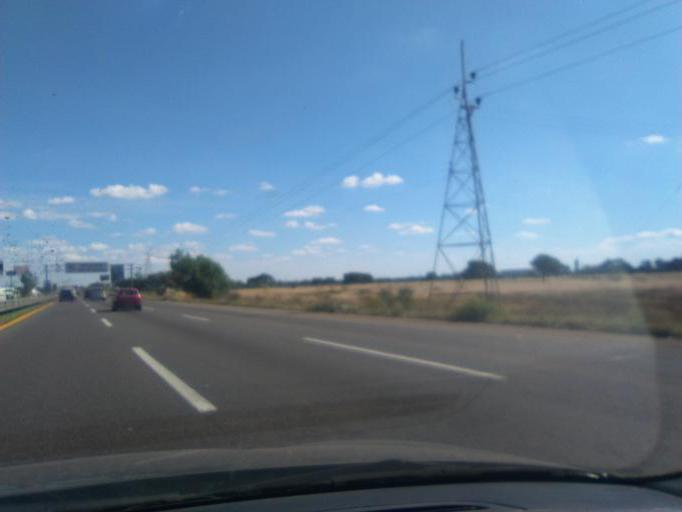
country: MX
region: Guanajuato
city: Silao
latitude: 20.9644
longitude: -101.4545
